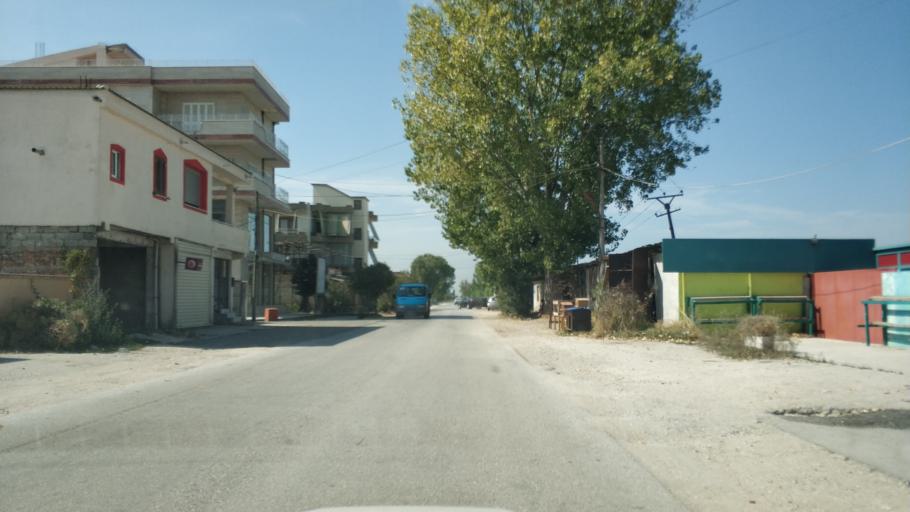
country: AL
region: Fier
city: Fier
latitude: 40.7285
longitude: 19.5475
